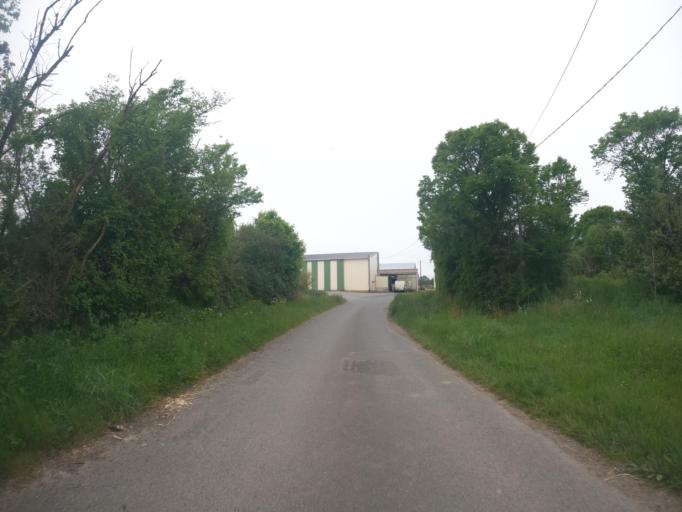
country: FR
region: Poitou-Charentes
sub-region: Departement des Deux-Sevres
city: Saint-Varent
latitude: 46.8904
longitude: -0.3154
